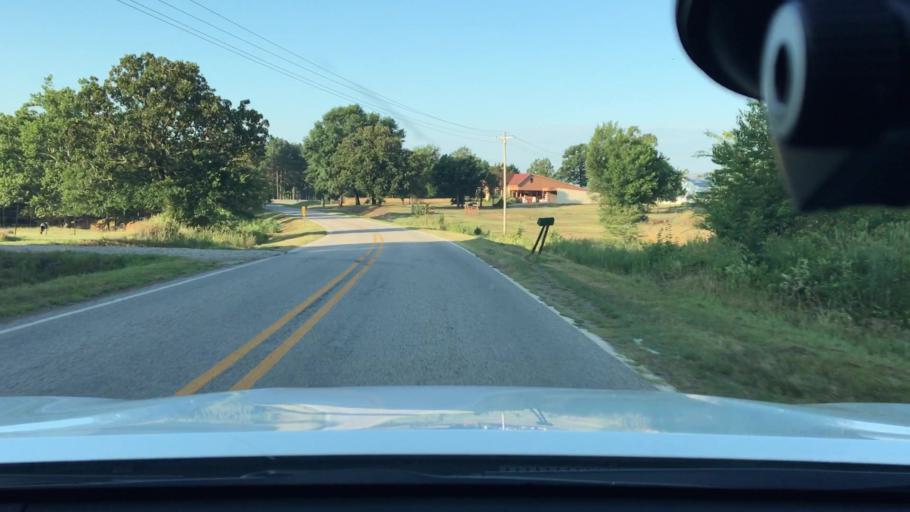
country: US
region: Arkansas
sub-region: Johnson County
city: Coal Hill
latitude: 35.3435
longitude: -93.5960
